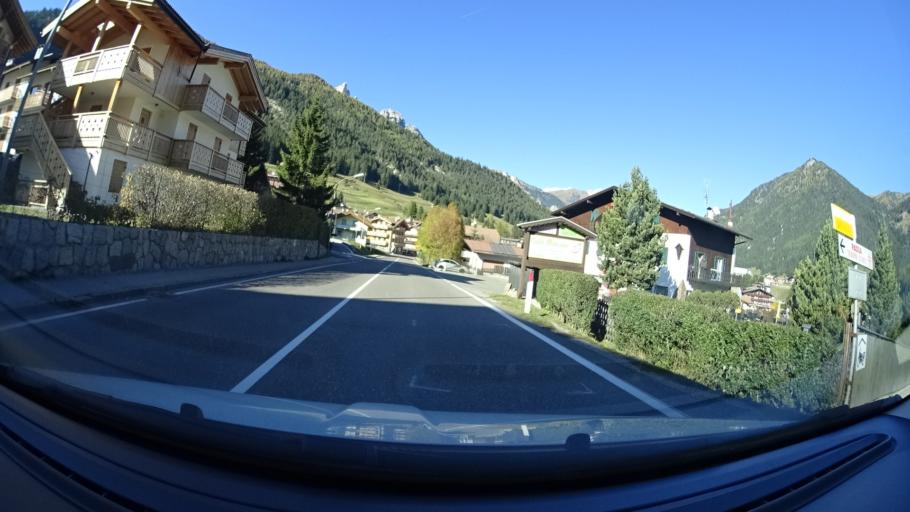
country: IT
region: Trentino-Alto Adige
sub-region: Provincia di Trento
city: Pozza di Fassa
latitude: 46.4253
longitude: 11.6828
